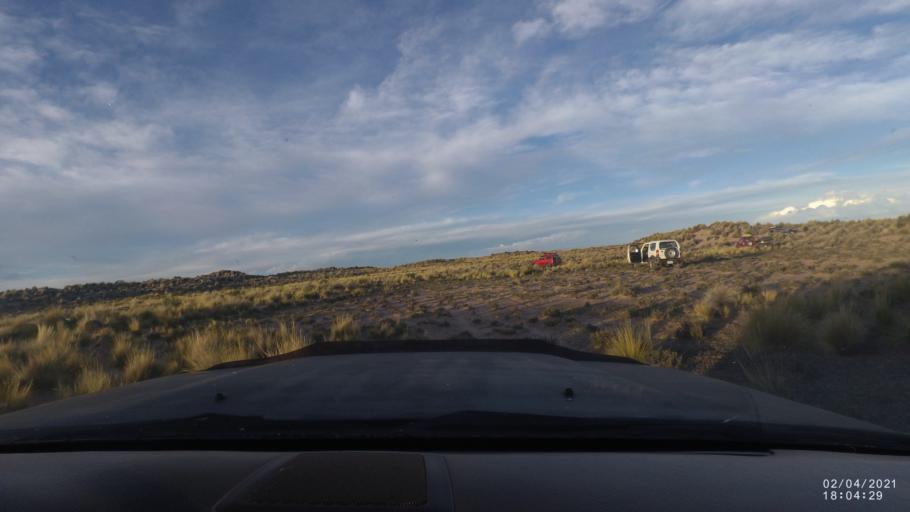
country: BO
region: Oruro
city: Poopo
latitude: -18.7105
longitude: -67.5401
